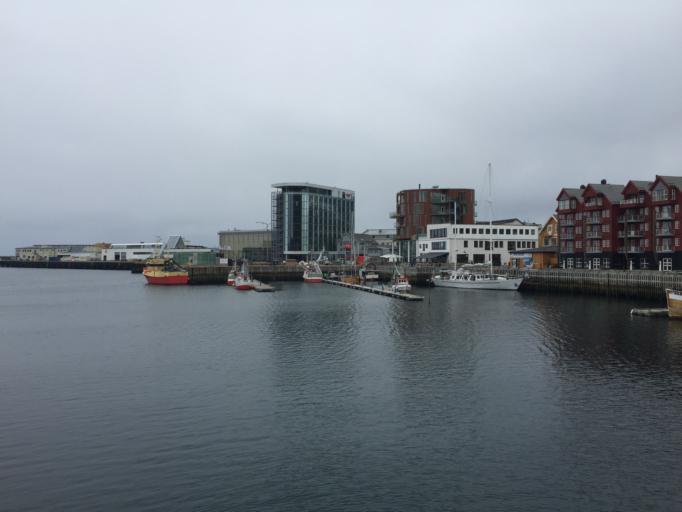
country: NO
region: Nordland
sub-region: Vagan
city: Svolvaer
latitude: 68.2334
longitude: 14.5695
